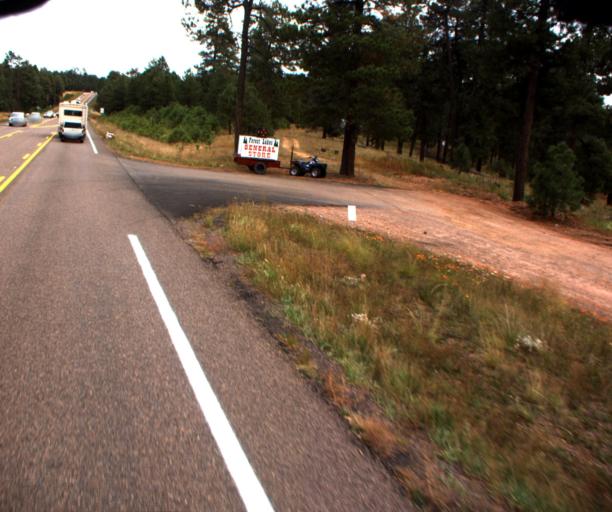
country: US
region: Arizona
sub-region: Navajo County
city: Heber-Overgaard
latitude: 34.3299
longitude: -110.8018
